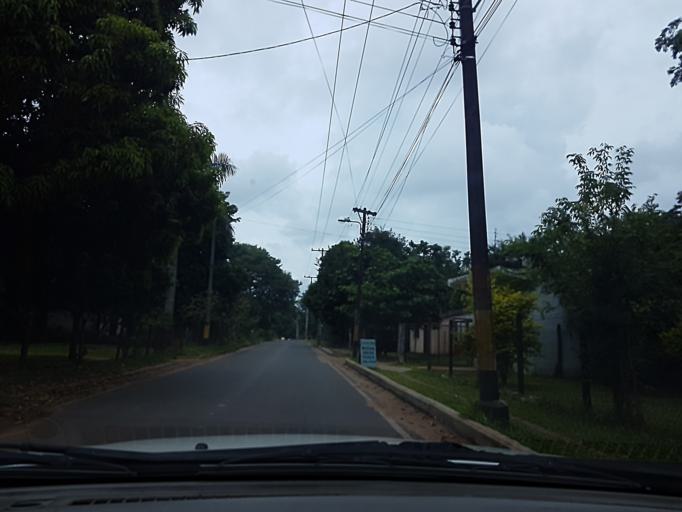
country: PY
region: Central
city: Limpio
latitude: -25.1843
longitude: -57.4680
